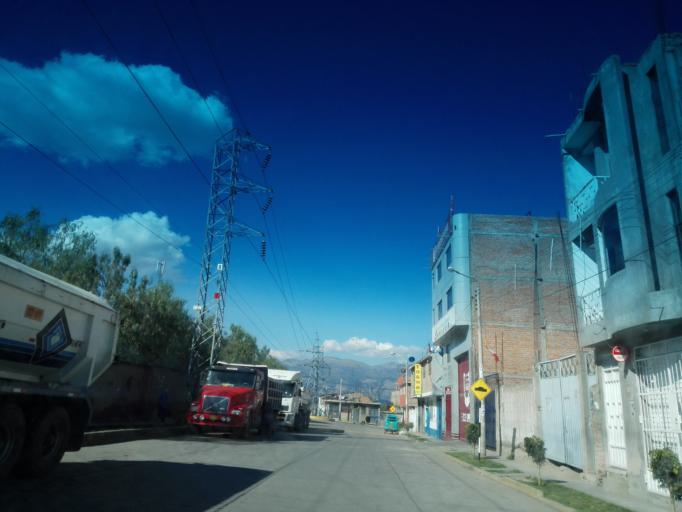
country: PE
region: Ayacucho
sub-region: Provincia de Huamanga
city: Ayacucho
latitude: -13.1489
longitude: -74.2154
